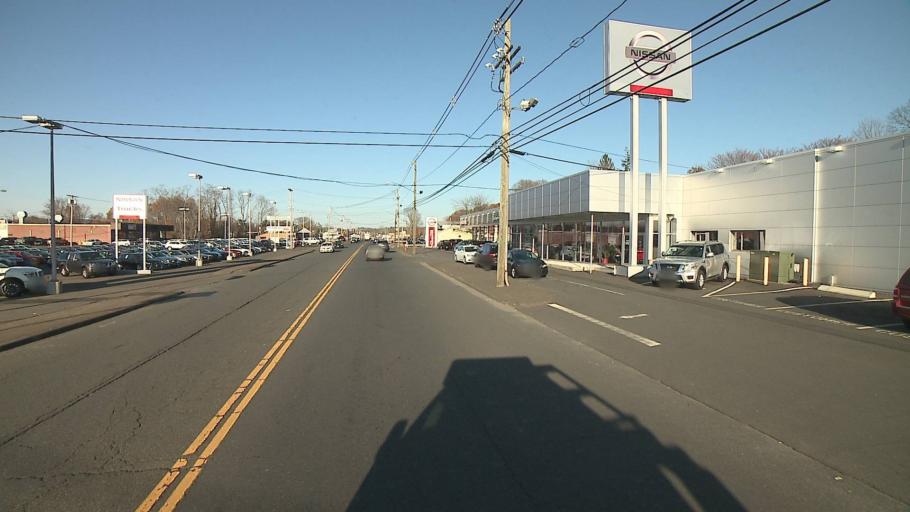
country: US
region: Connecticut
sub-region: New Haven County
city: Wallingford
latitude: 41.4673
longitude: -72.8181
